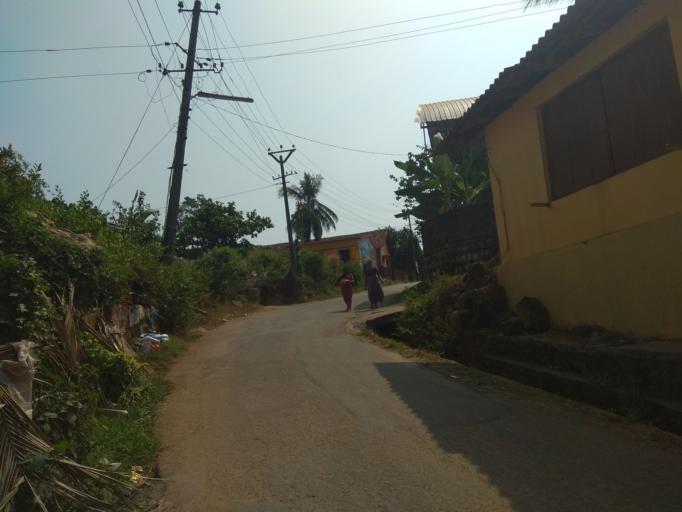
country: IN
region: Karnataka
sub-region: Dakshina Kannada
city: Mangalore
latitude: 12.9270
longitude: 74.8438
